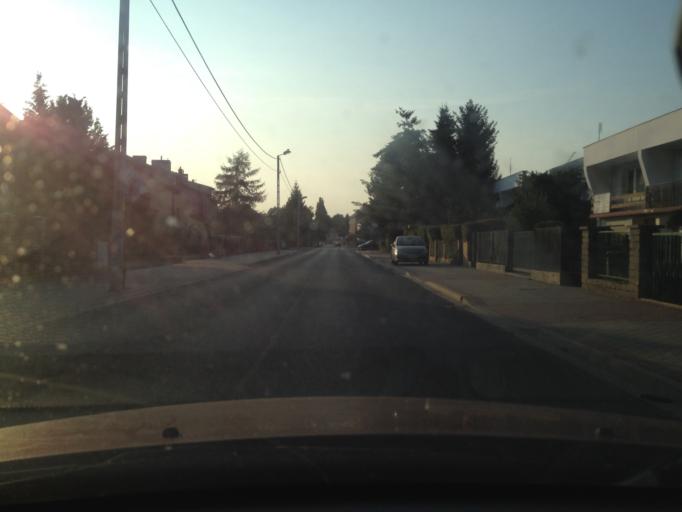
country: PL
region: Lower Silesian Voivodeship
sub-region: Powiat zgorzelecki
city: Zgorzelec
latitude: 51.1353
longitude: 15.0196
